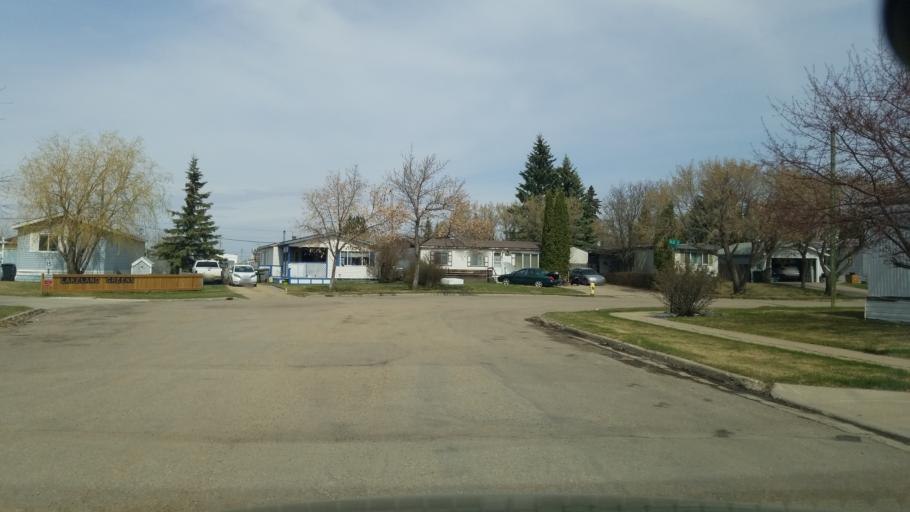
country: CA
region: Saskatchewan
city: Lloydminster
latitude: 53.2918
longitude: -110.0123
